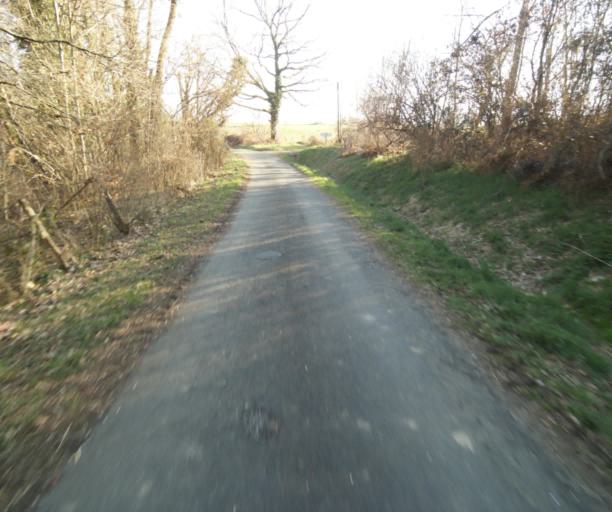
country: FR
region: Limousin
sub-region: Departement de la Correze
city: Saint-Clement
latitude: 45.3484
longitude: 1.6708
